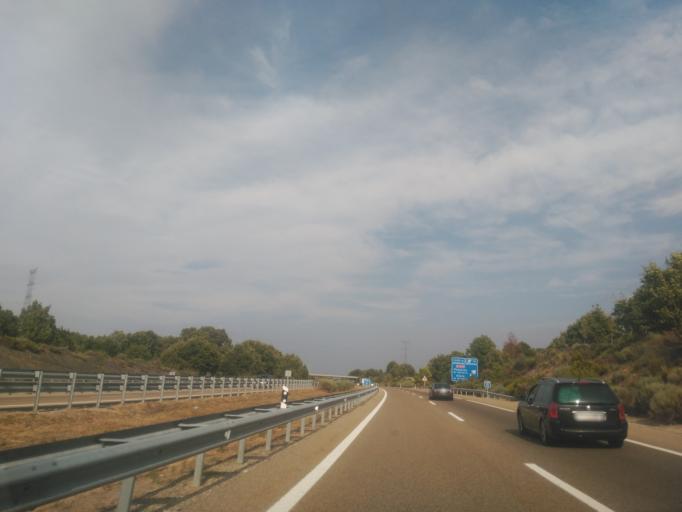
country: ES
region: Castille and Leon
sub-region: Provincia de Zamora
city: Robleda-Cervantes
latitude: 42.0549
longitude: -6.5791
